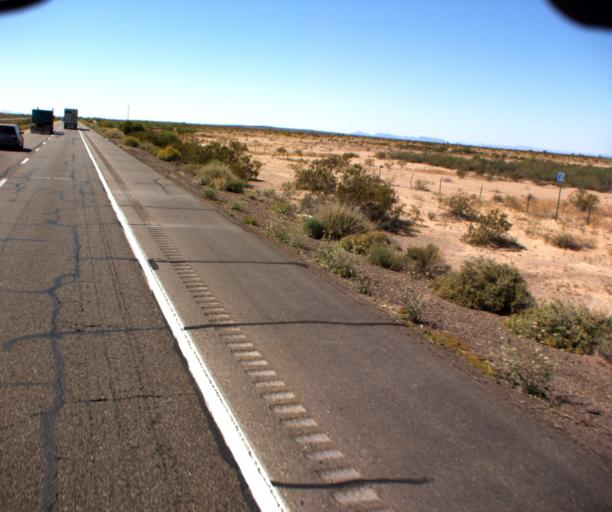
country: US
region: Arizona
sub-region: Maricopa County
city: Gila Bend
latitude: 32.8621
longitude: -113.1773
